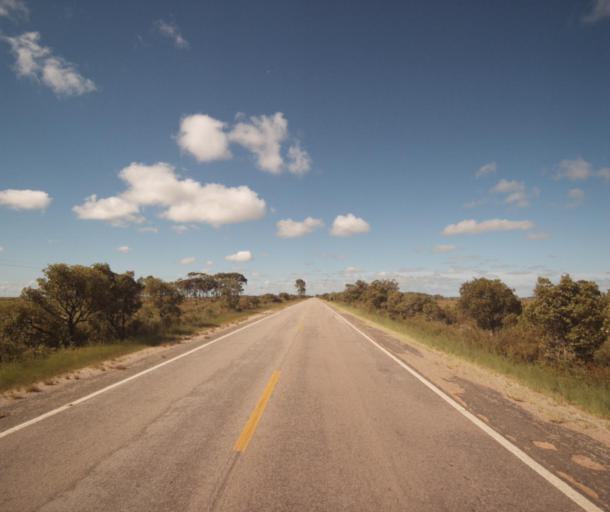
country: BR
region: Rio Grande do Sul
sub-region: Santa Vitoria Do Palmar
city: Santa Vitoria do Palmar
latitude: -33.3829
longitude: -53.2000
